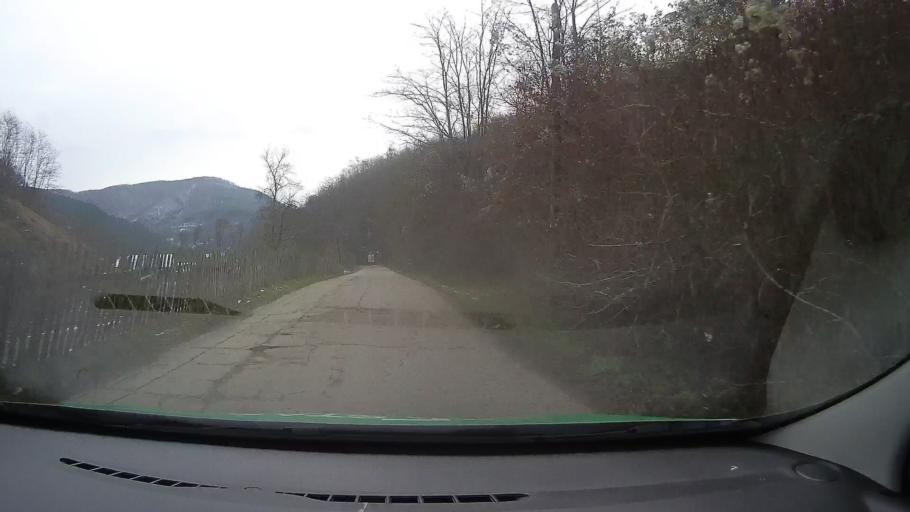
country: RO
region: Hunedoara
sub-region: Comuna Balsa
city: Balsa
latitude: 45.9810
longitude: 23.1643
